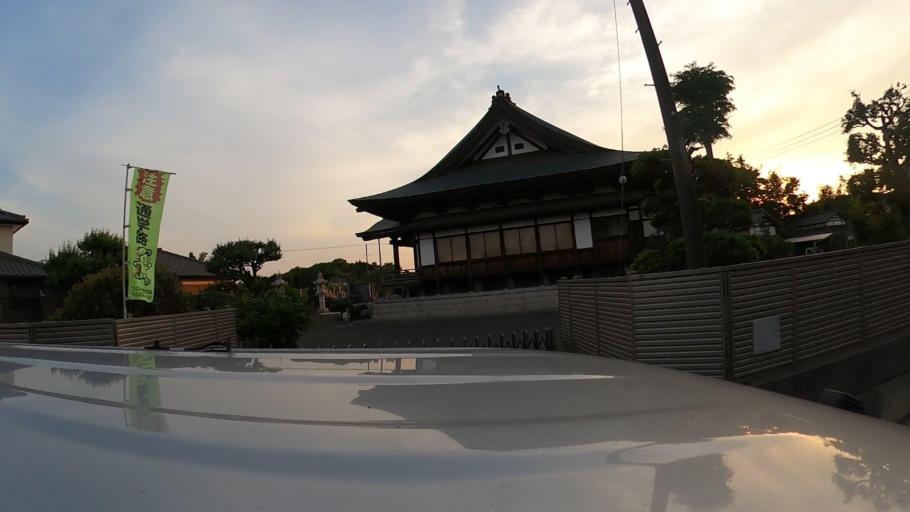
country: JP
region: Ibaraki
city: Ushiku
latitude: 36.0258
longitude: 140.0925
